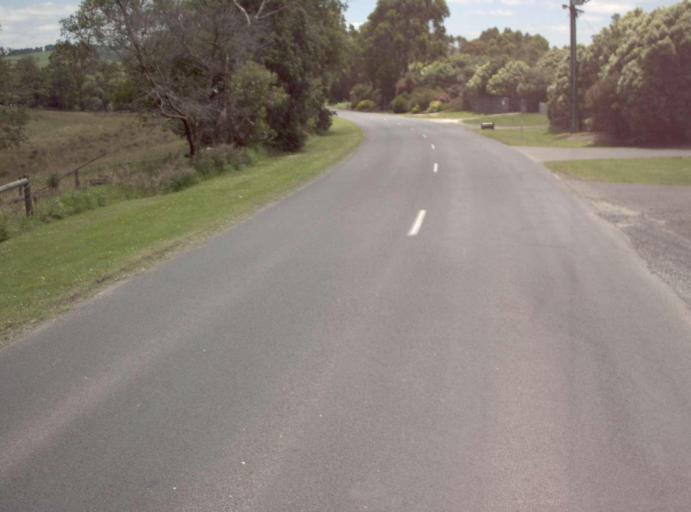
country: AU
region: Victoria
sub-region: Bass Coast
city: North Wonthaggi
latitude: -38.6999
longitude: 146.0879
